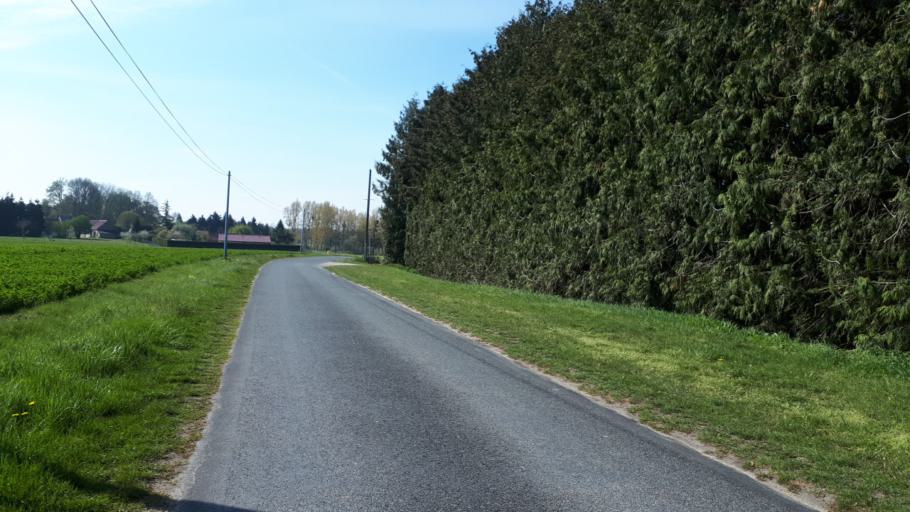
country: FR
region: Centre
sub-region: Departement du Loir-et-Cher
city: Contres
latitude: 47.3859
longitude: 1.3782
